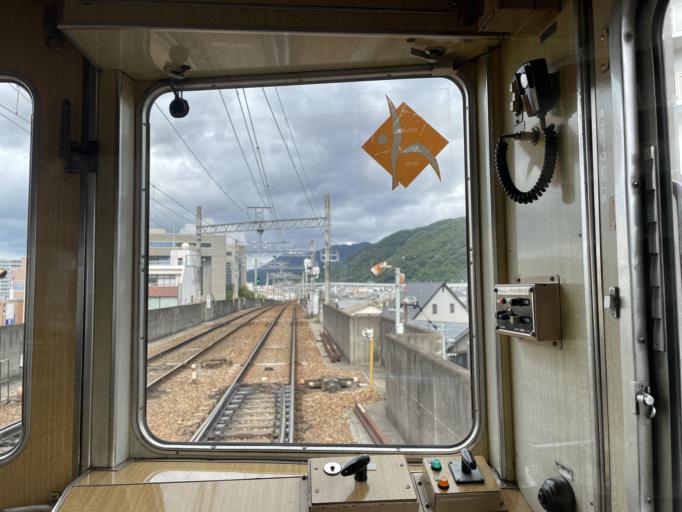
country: JP
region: Hyogo
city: Kawanishi
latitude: 34.8286
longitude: 135.4161
